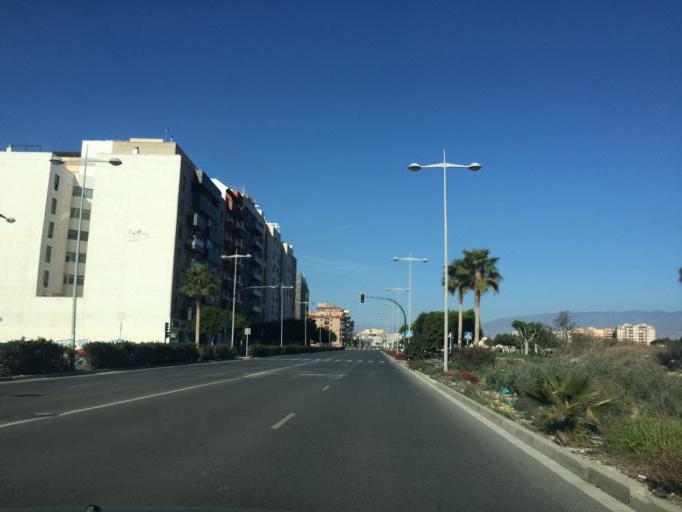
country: ES
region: Andalusia
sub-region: Provincia de Almeria
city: Almeria
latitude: 36.8299
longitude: -2.4379
